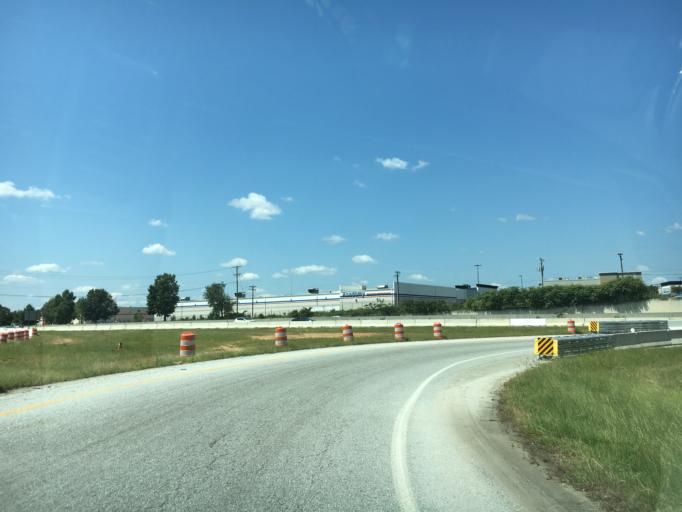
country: US
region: South Carolina
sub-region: Greenville County
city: Mauldin
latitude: 34.8281
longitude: -82.3033
